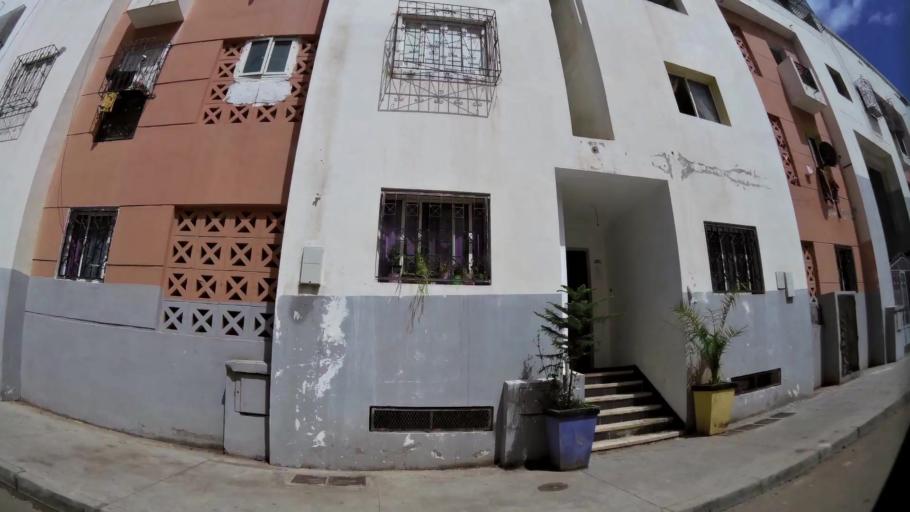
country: MA
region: Grand Casablanca
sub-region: Mediouna
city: Tit Mellil
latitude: 33.6081
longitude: -7.4851
